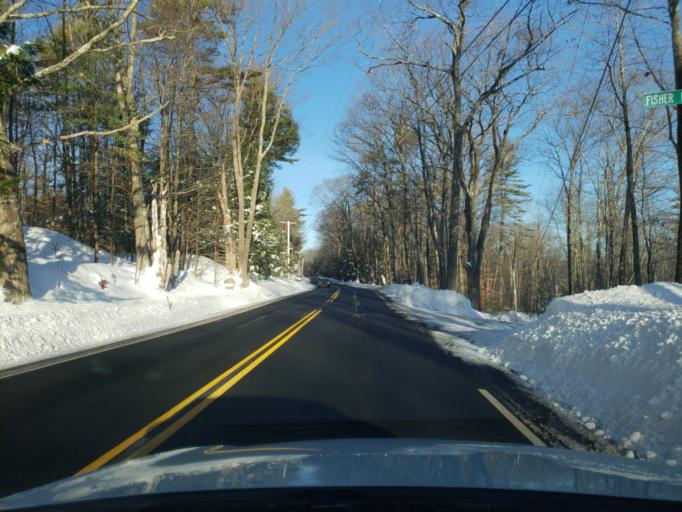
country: US
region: New Hampshire
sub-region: Hillsborough County
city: Greenfield
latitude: 43.0058
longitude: -71.8345
